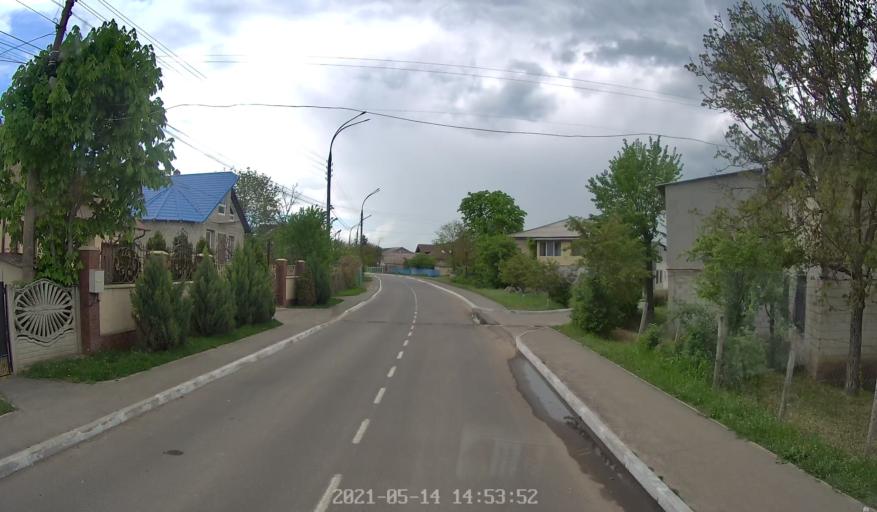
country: MD
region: Hincesti
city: Hincesti
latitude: 46.8243
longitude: 28.5974
